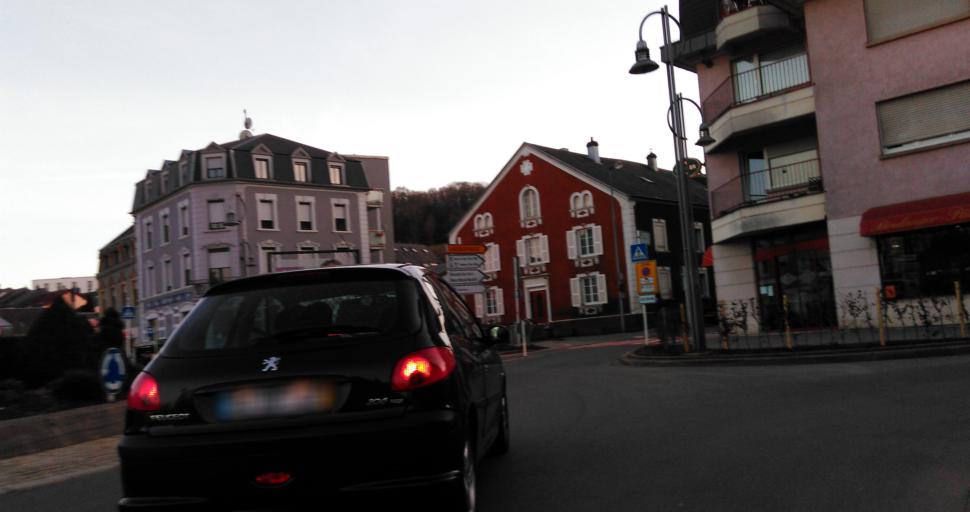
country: LU
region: Luxembourg
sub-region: Canton d'Esch-sur-Alzette
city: Niedercorn
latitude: 49.5353
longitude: 5.8912
